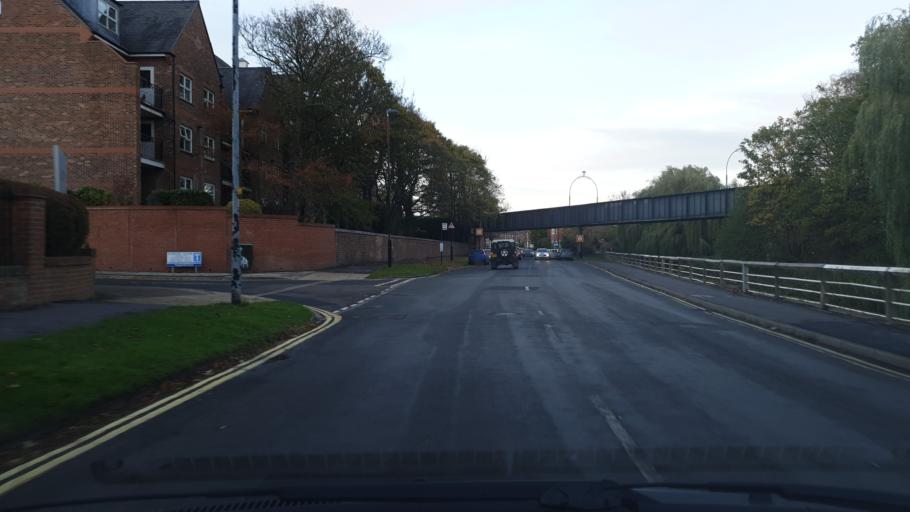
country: GB
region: England
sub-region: City of York
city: York
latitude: 53.9703
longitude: -1.0735
